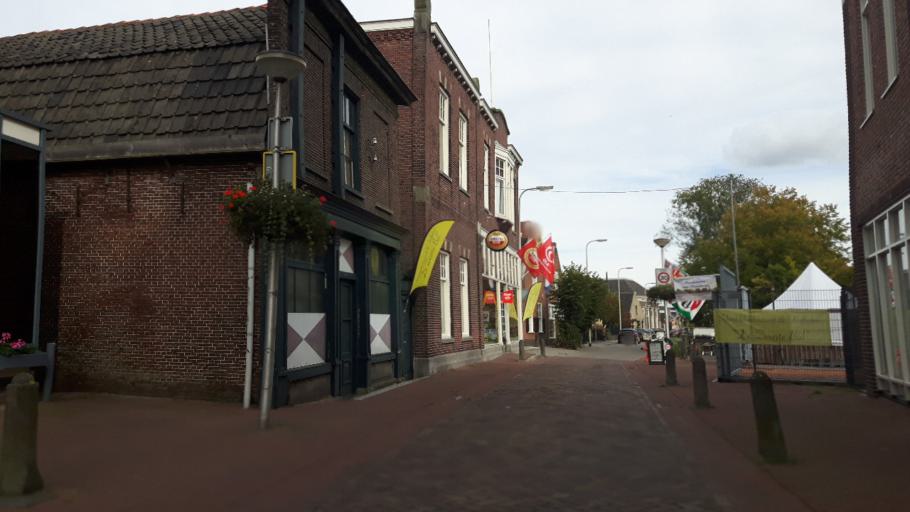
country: NL
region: South Holland
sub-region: Gemeente Nieuwkoop
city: Nieuwkoop
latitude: 52.1506
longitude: 4.7798
